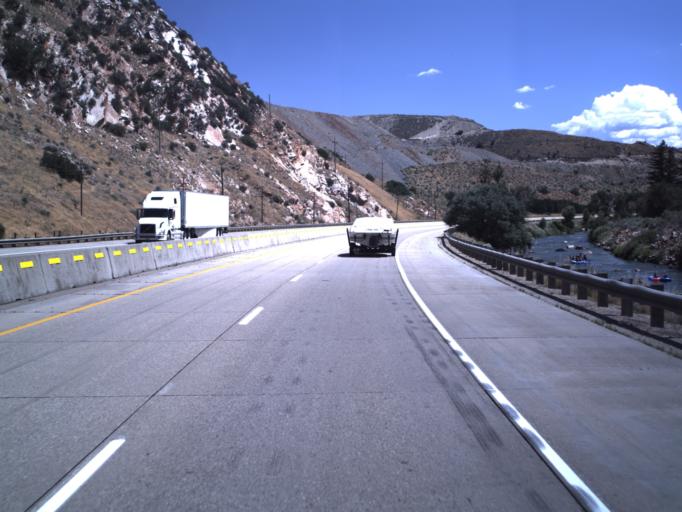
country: US
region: Utah
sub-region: Morgan County
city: Morgan
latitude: 41.0652
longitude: -111.5554
